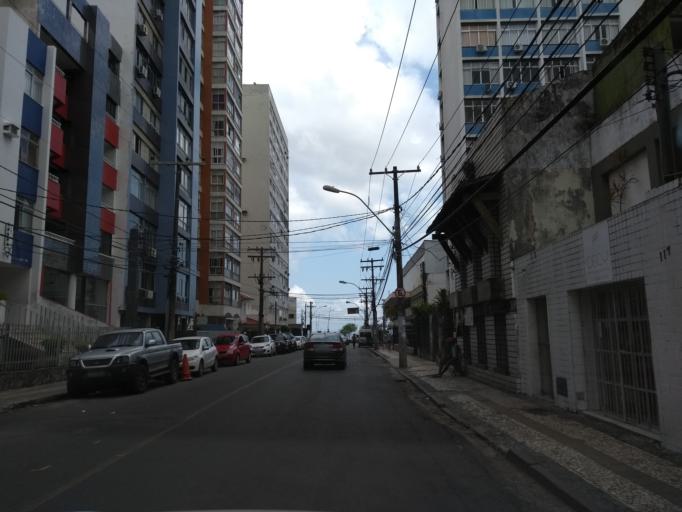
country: BR
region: Bahia
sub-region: Salvador
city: Salvador
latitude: -13.0032
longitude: -38.5311
